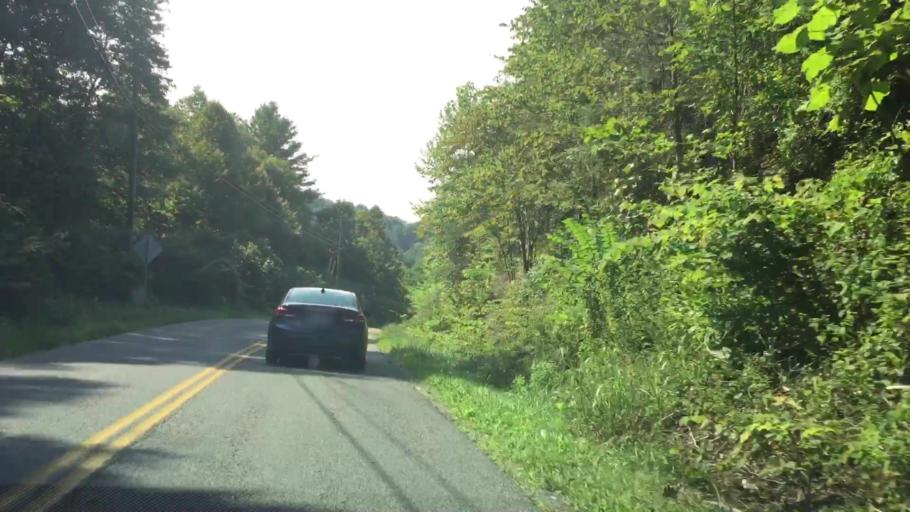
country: US
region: Tennessee
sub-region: Sullivan County
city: Fairmount
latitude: 36.6038
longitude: -82.0720
